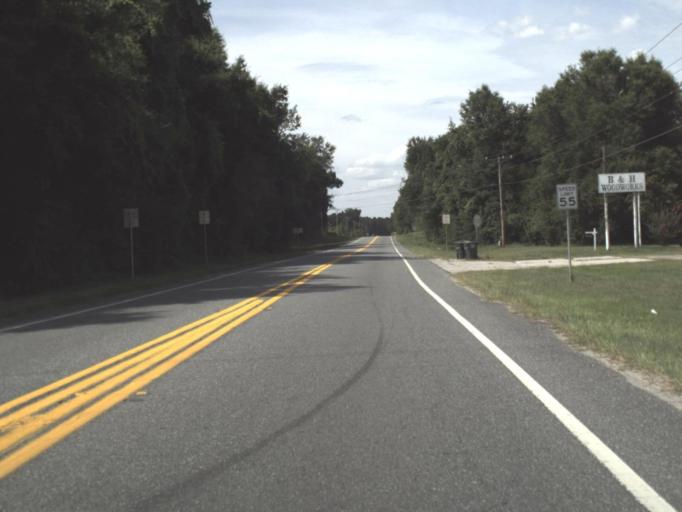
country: US
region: Florida
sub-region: Columbia County
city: Lake City
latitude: 30.0713
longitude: -82.6969
